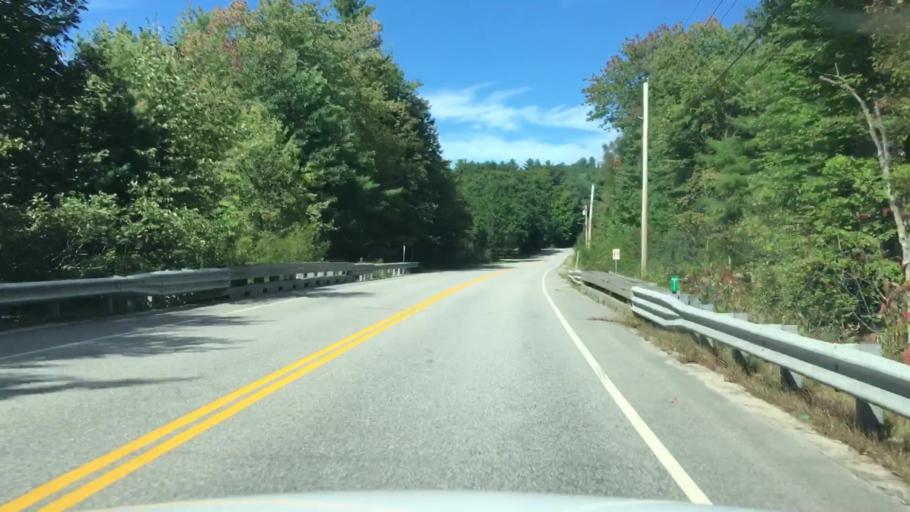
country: US
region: Maine
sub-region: Cumberland County
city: West Scarborough
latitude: 43.6274
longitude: -70.4087
